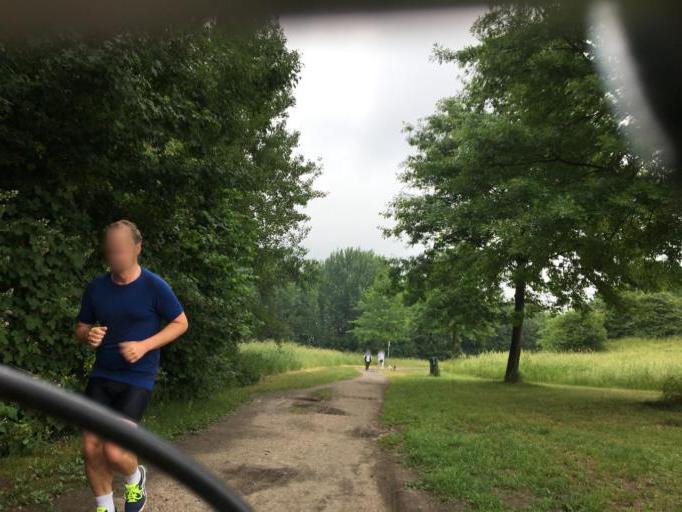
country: DE
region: Hamburg
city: Eidelstedt
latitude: 53.5767
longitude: 9.8707
